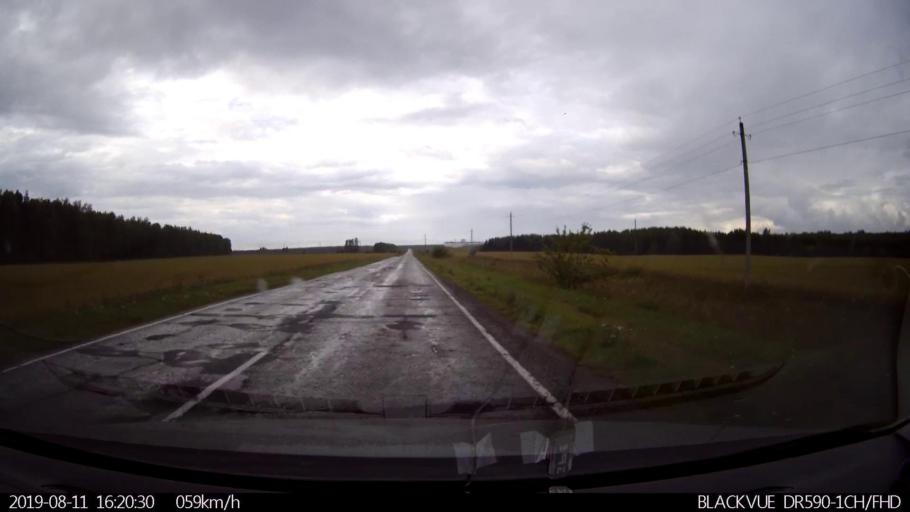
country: RU
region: Ulyanovsk
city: Mayna
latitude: 54.0722
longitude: 47.6027
